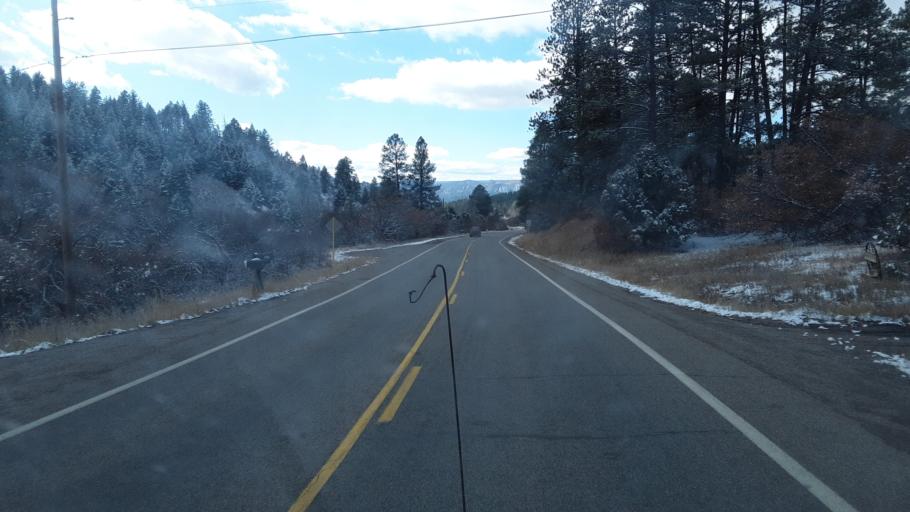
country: US
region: Colorado
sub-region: La Plata County
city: Durango
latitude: 37.3132
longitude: -107.8022
